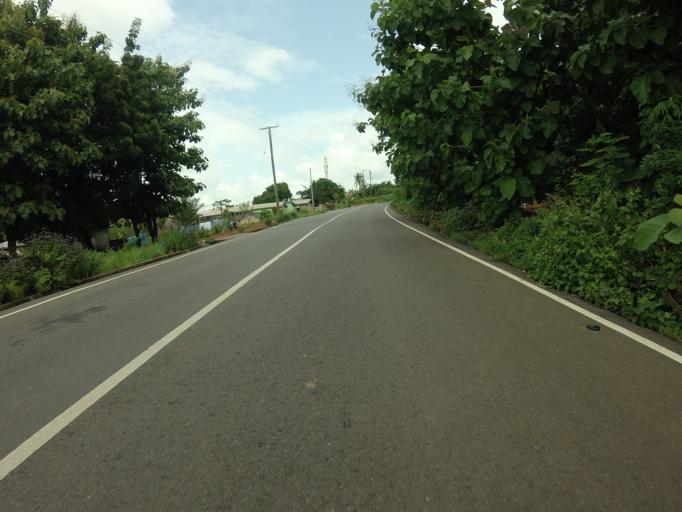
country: GH
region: Volta
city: Ho
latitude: 6.6133
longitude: 0.4587
